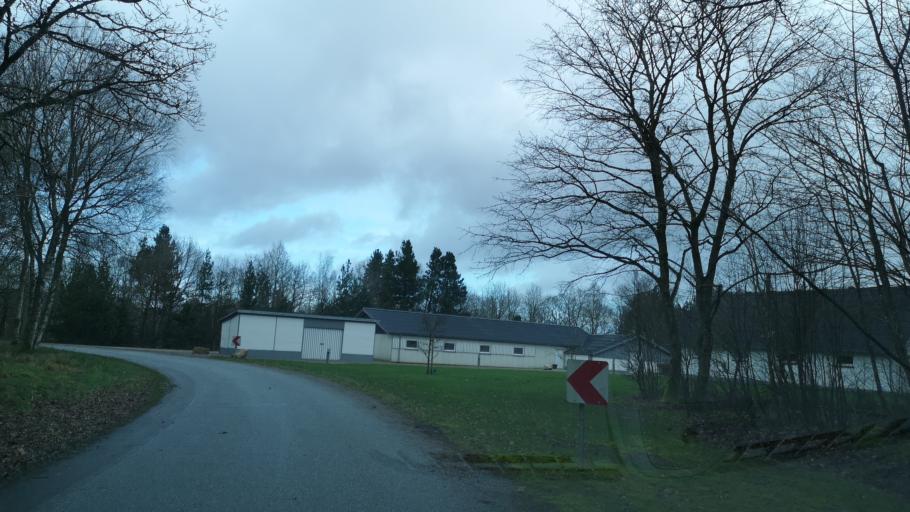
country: DK
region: Central Jutland
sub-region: Herning Kommune
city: Lind
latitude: 56.0007
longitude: 8.9712
